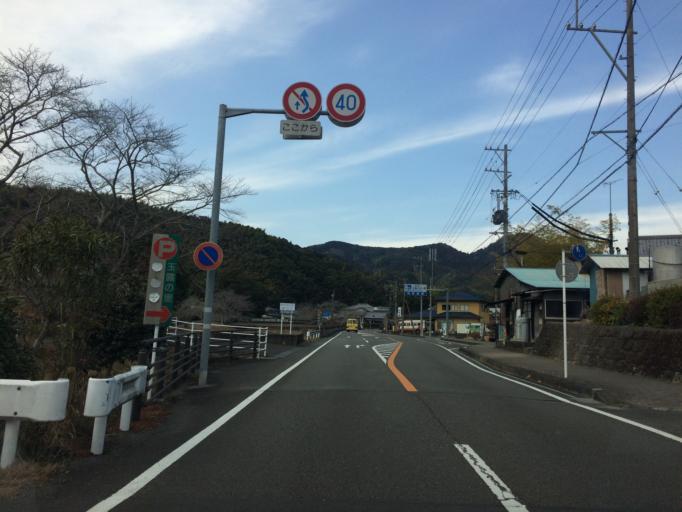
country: JP
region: Shizuoka
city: Fujieda
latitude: 34.9502
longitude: 138.2517
